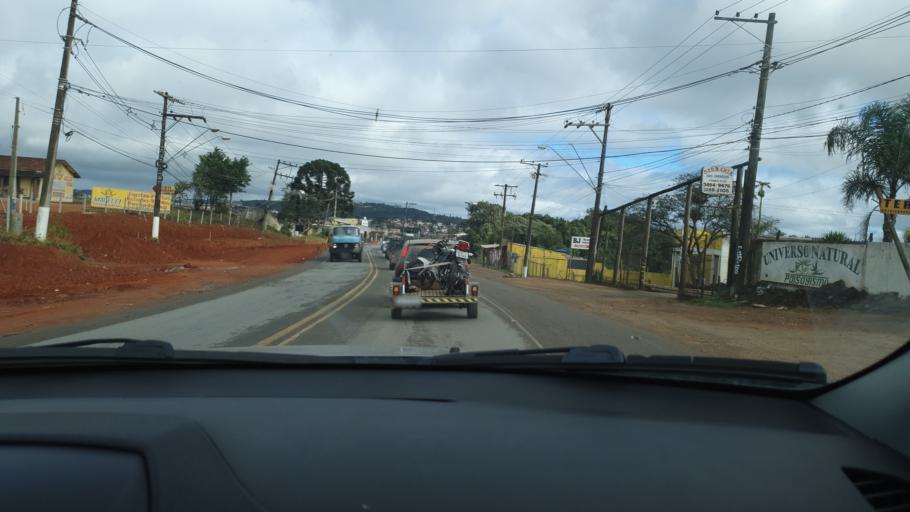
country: BR
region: Sao Paulo
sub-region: Ibiuna
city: Ibiuna
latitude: -23.6568
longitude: -47.2012
